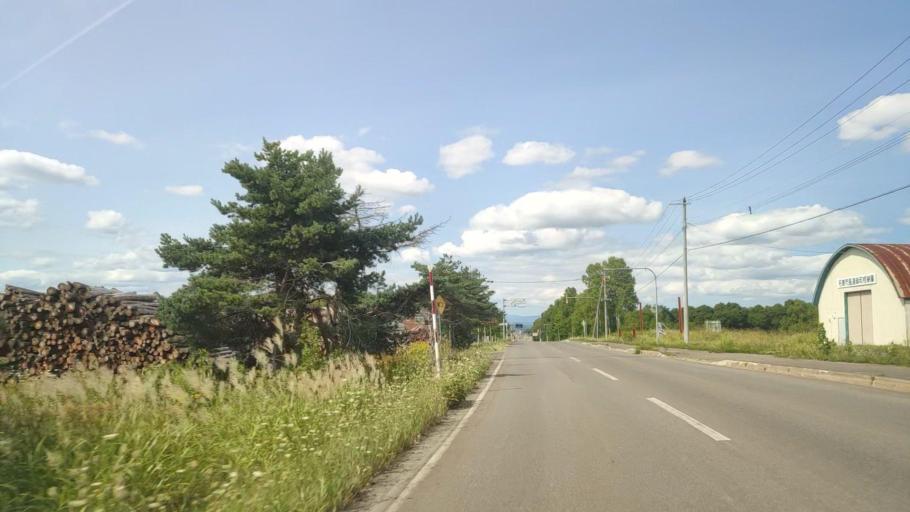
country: JP
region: Hokkaido
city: Nayoro
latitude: 44.2841
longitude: 142.4295
